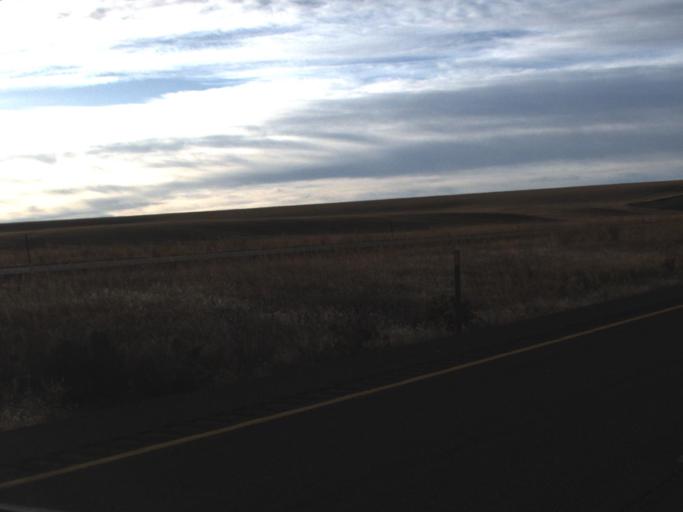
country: US
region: Washington
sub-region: Adams County
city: Ritzville
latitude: 47.0681
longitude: -118.4100
